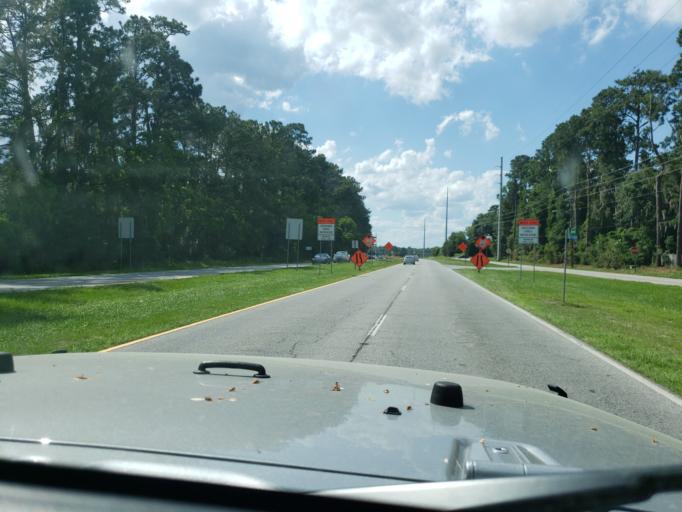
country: US
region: Georgia
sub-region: Chatham County
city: Whitemarsh Island
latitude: 32.0551
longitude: -81.0170
